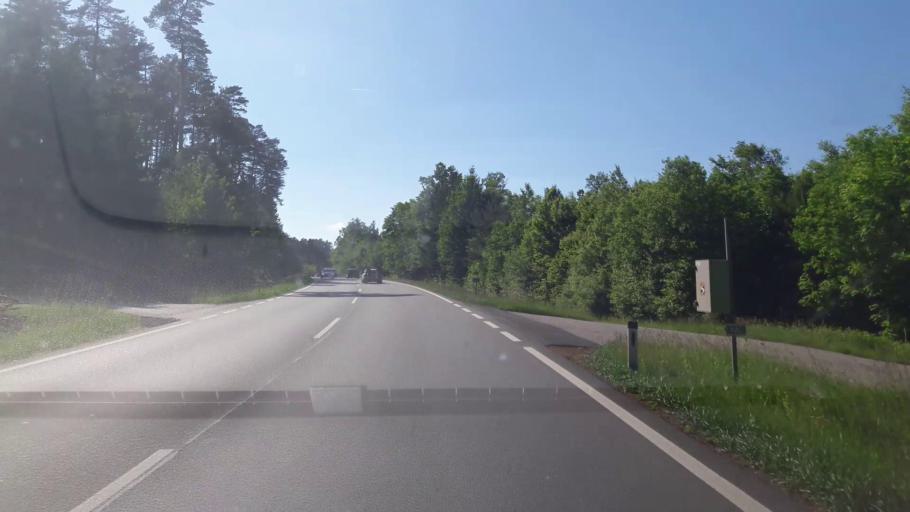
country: AT
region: Burgenland
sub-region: Politischer Bezirk Oberwart
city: Kemeten
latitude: 47.2796
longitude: 16.1512
